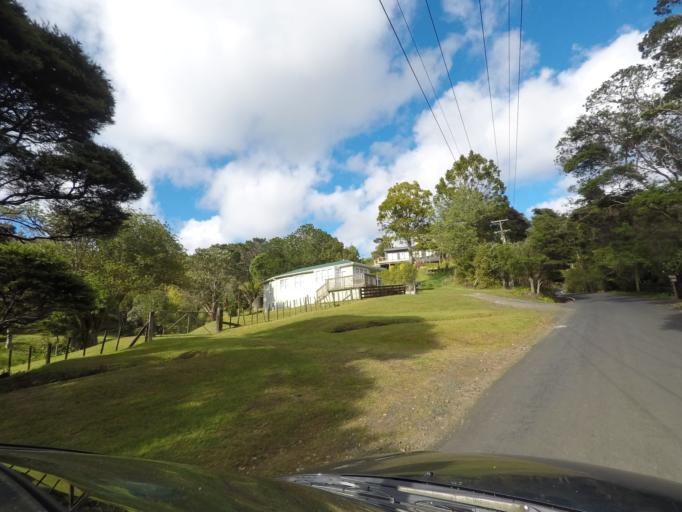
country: NZ
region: Auckland
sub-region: Auckland
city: Titirangi
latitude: -37.0165
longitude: 174.5552
